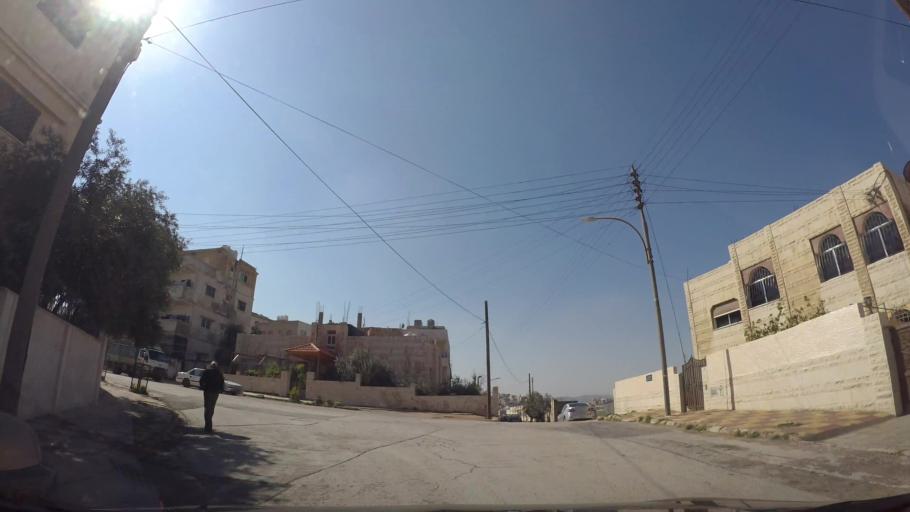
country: JO
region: Amman
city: Amman
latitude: 31.9854
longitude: 35.9797
